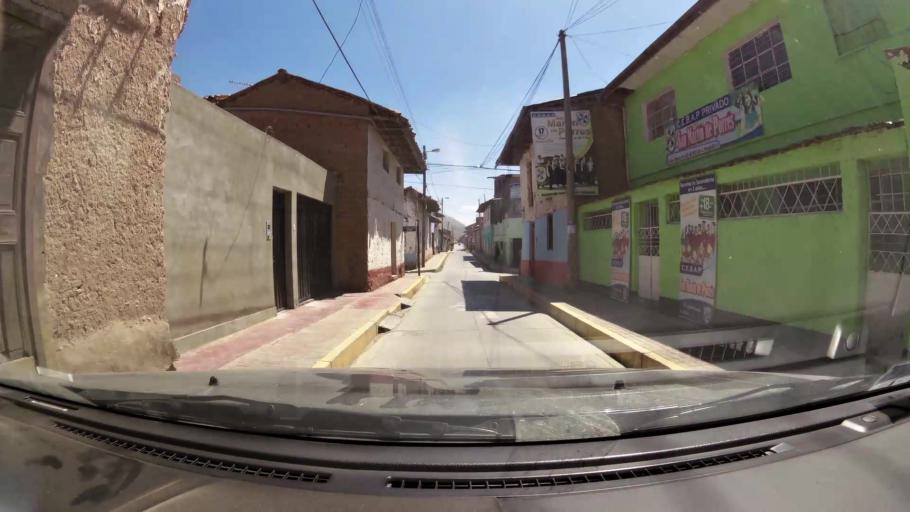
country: PE
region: Junin
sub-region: Provincia de Jauja
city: Jauja
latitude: -11.7715
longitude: -75.4994
